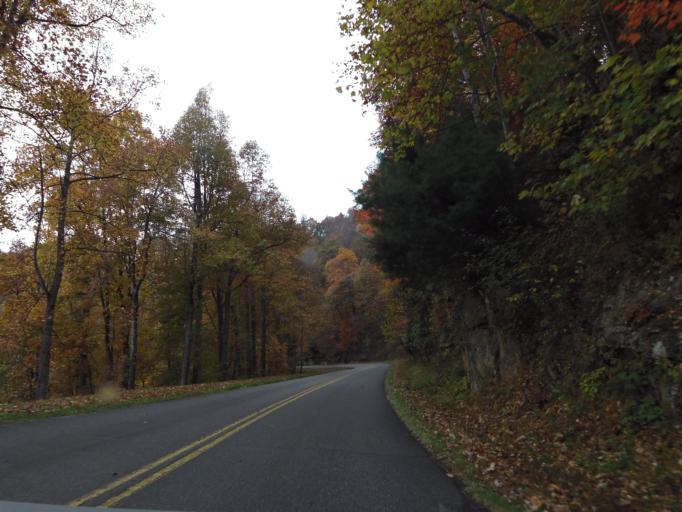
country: US
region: North Carolina
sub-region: Ashe County
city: West Jefferson
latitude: 36.2598
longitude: -81.4440
